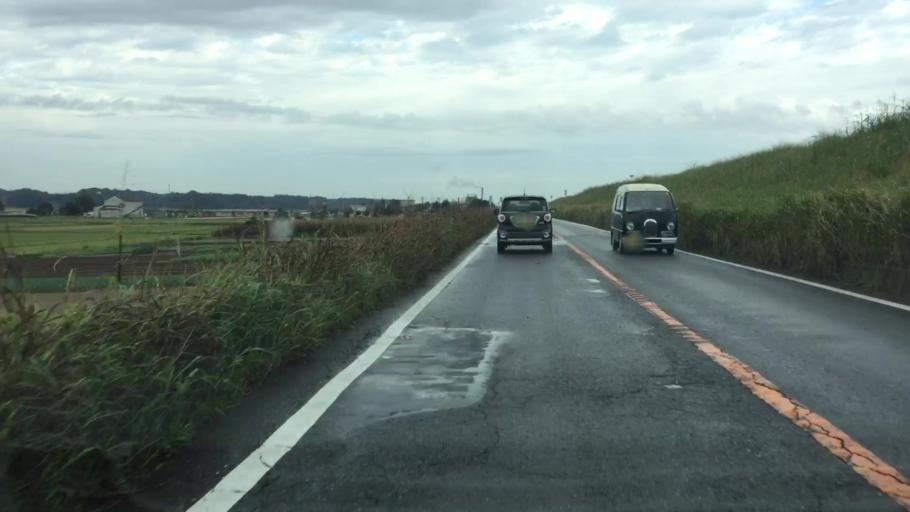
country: JP
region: Ibaraki
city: Toride
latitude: 35.8713
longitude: 140.1155
